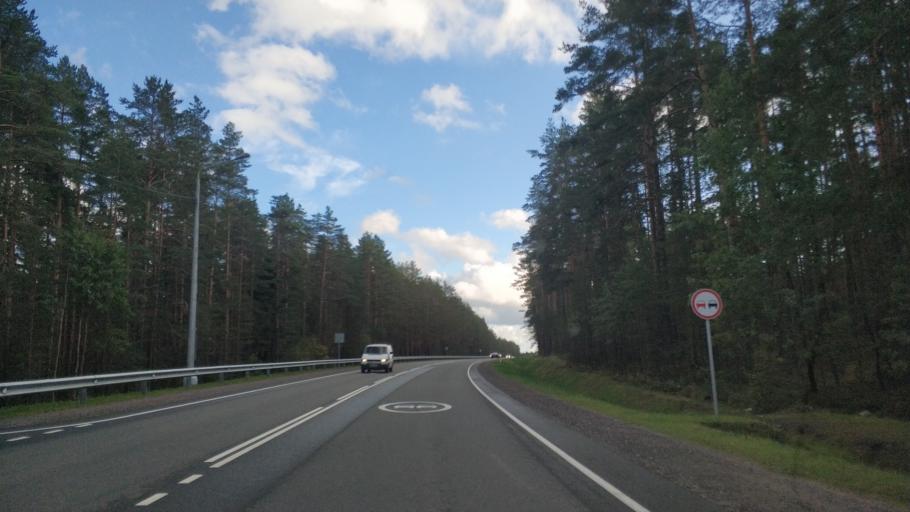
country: RU
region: Leningrad
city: Priozersk
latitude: 60.9934
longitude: 30.1830
